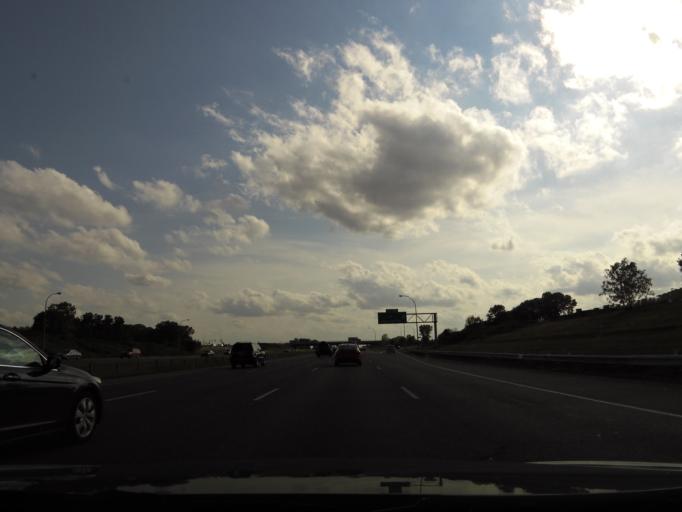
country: US
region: Minnesota
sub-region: Dakota County
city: Mendota Heights
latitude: 44.8524
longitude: -93.1501
